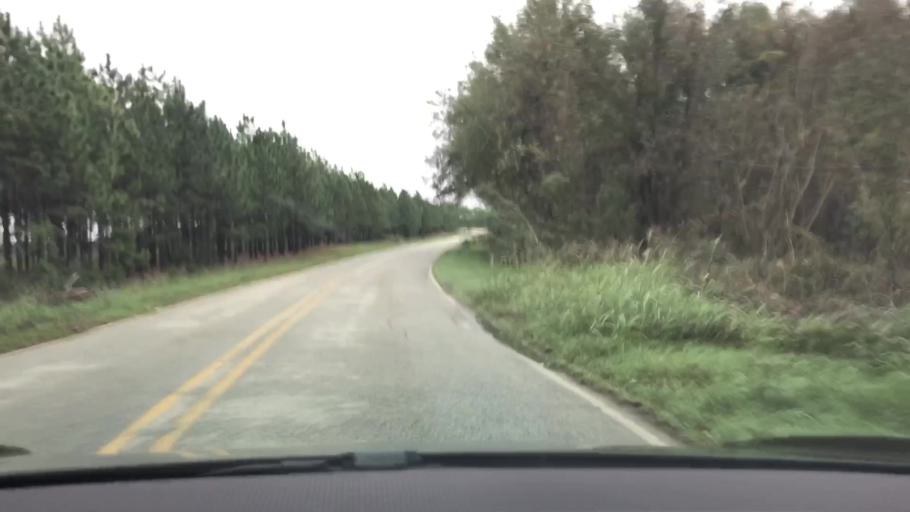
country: US
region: Georgia
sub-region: Jefferson County
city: Wadley
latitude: 32.8382
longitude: -82.3913
